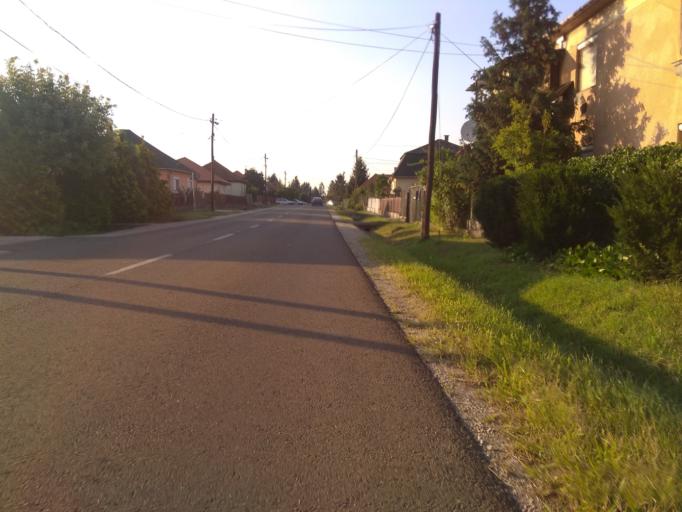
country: HU
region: Borsod-Abauj-Zemplen
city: Nyekladhaza
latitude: 47.9878
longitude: 20.8388
